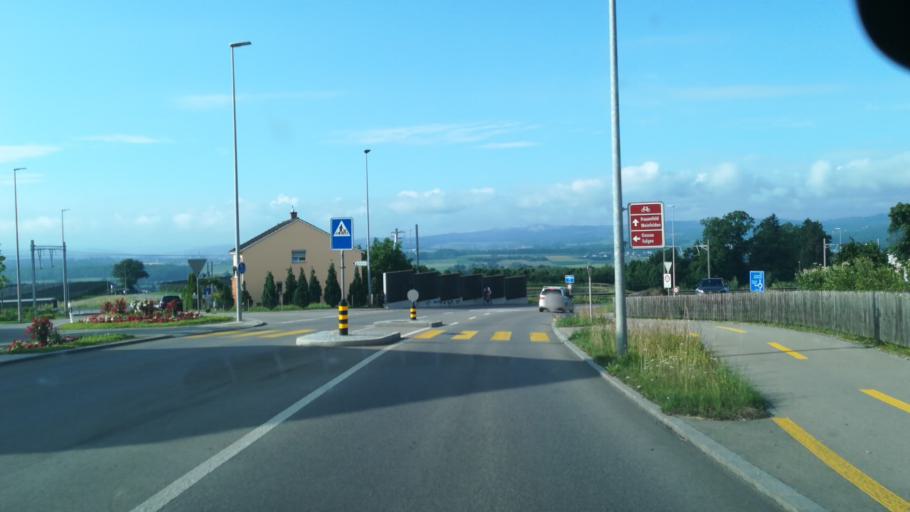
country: CH
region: Thurgau
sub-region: Weinfelden District
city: Berg
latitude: 47.5728
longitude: 9.1682
